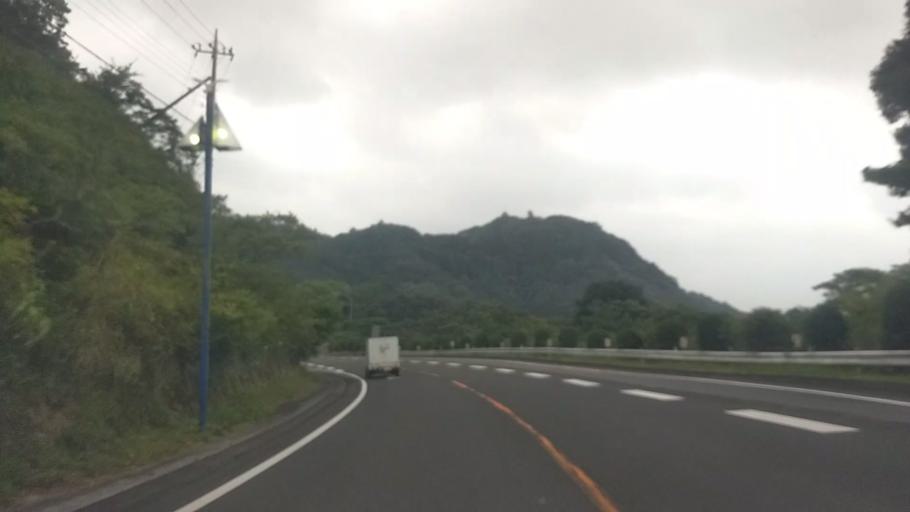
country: JP
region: Chiba
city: Kawaguchi
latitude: 35.1587
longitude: 140.0661
